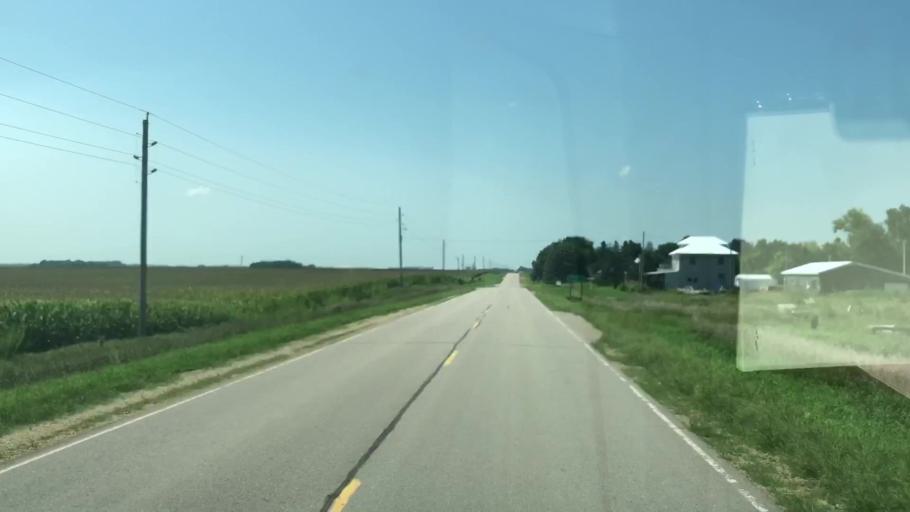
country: US
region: Iowa
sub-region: O'Brien County
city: Sheldon
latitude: 43.2443
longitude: -95.7799
